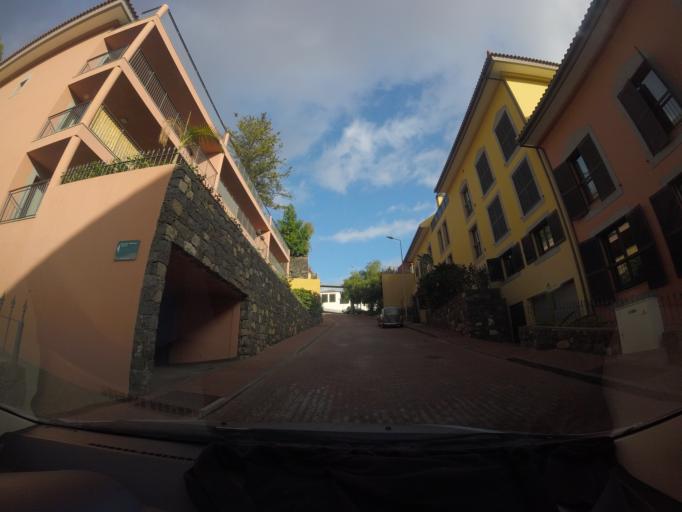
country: PT
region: Madeira
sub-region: Funchal
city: Nossa Senhora do Monte
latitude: 32.6561
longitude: -16.9088
